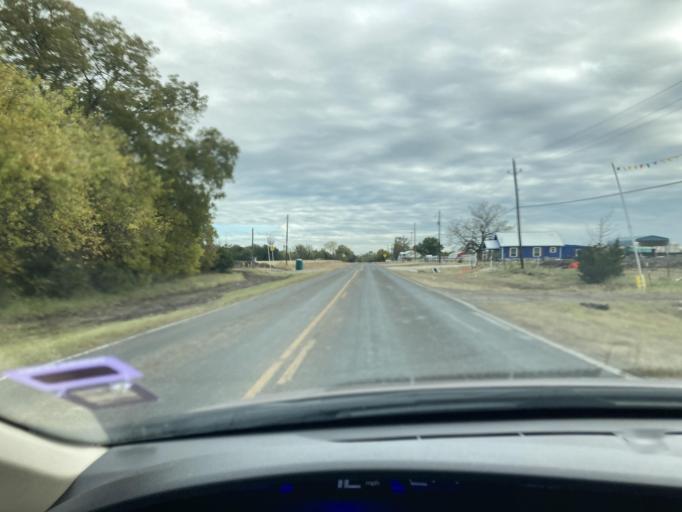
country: US
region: Texas
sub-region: Navarro County
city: Corsicana
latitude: 32.0652
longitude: -96.5016
